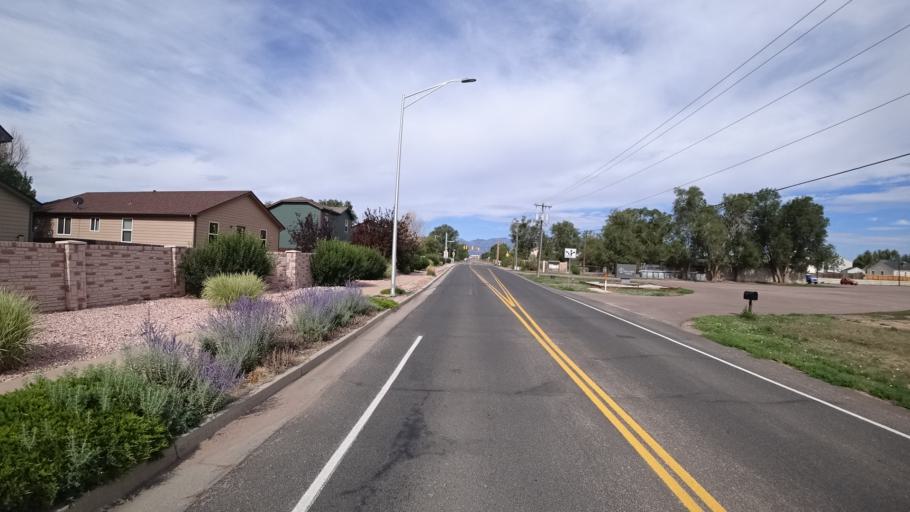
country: US
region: Colorado
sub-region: El Paso County
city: Fountain
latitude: 38.7084
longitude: -104.6953
